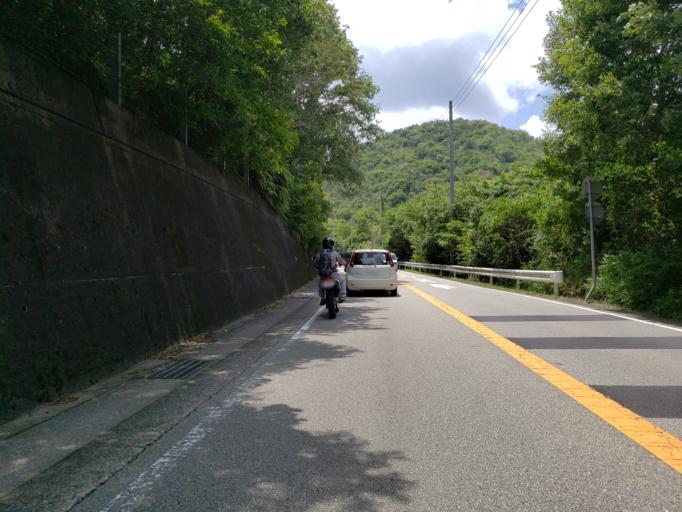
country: JP
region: Hyogo
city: Aioi
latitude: 34.7917
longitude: 134.4464
